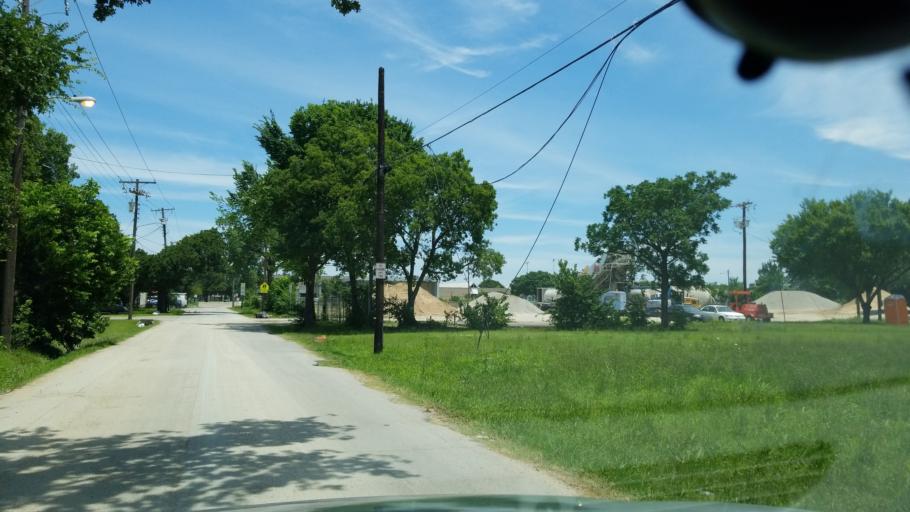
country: US
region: Texas
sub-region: Dallas County
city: Irving
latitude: 32.8197
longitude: -96.9463
